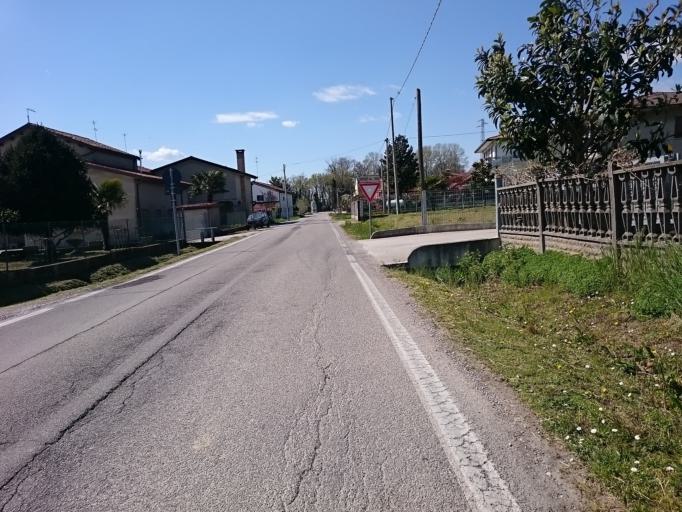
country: IT
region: Veneto
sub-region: Provincia di Padova
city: Brugine
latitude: 45.2914
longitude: 12.0007
